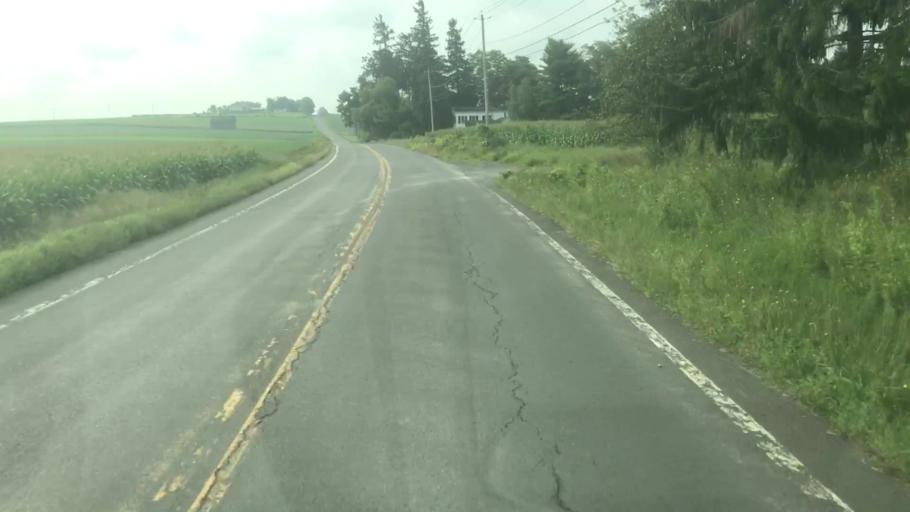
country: US
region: New York
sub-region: Onondaga County
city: Skaneateles
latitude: 42.8989
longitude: -76.4533
